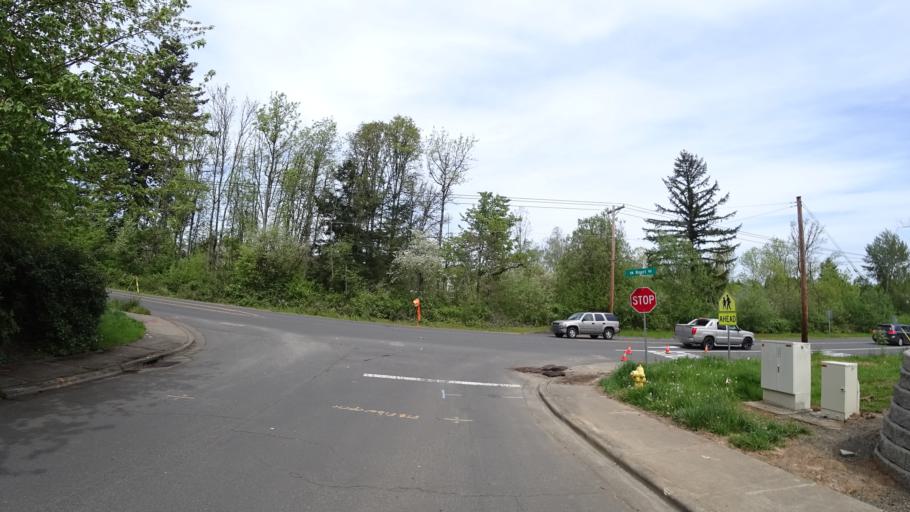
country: US
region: Oregon
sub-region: Washington County
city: Aloha
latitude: 45.4618
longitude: -122.8527
